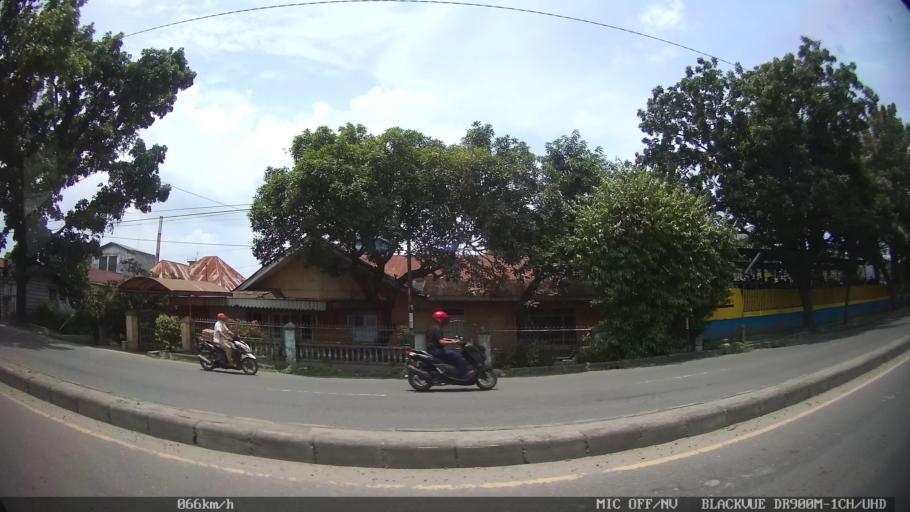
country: ID
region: North Sumatra
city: Labuhan Deli
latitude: 3.7125
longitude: 98.6794
